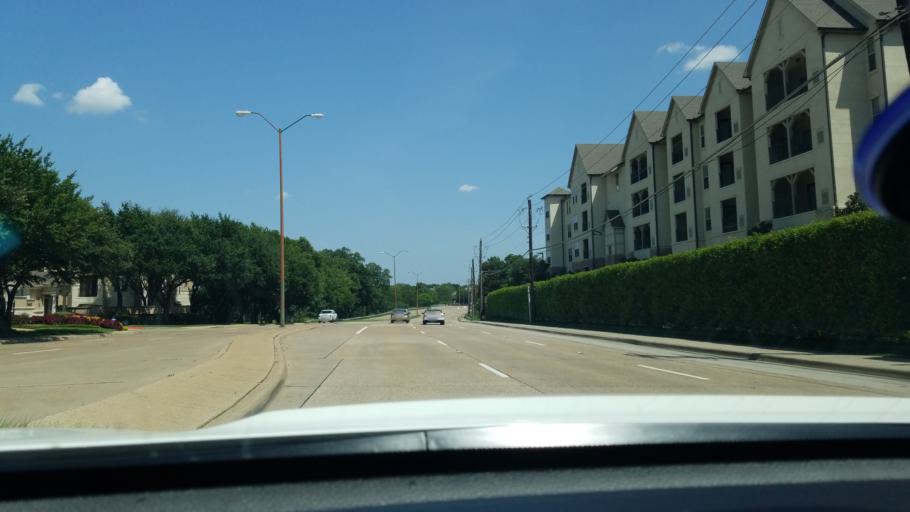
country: US
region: Texas
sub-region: Dallas County
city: Addison
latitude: 32.9612
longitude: -96.8141
